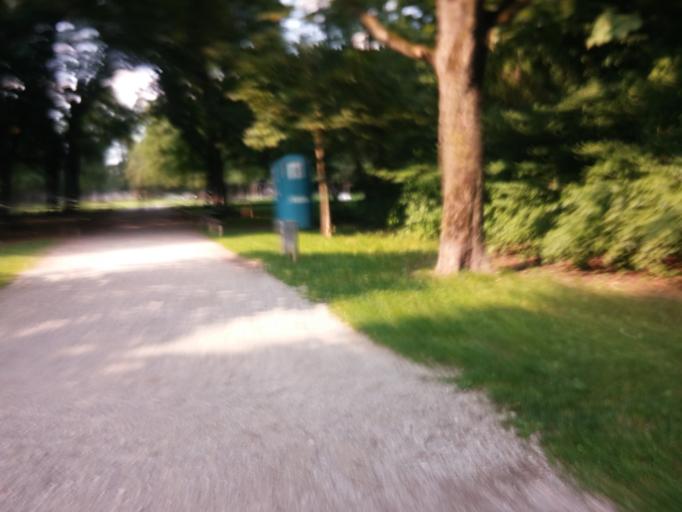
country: DE
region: Bavaria
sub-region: Upper Bavaria
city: Munich
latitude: 48.1656
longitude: 11.5682
